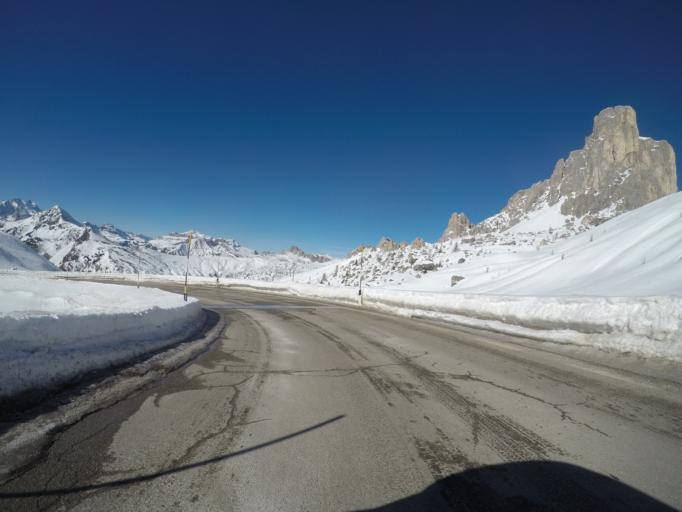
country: IT
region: Veneto
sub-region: Provincia di Belluno
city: Selva di Cadore
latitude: 46.4842
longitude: 12.0513
